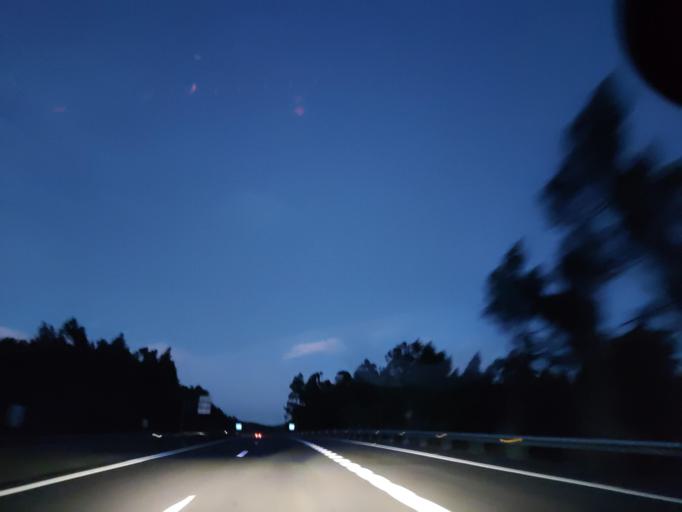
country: ES
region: Galicia
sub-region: Provincia da Coruna
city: Rois
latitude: 42.7295
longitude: -8.7062
